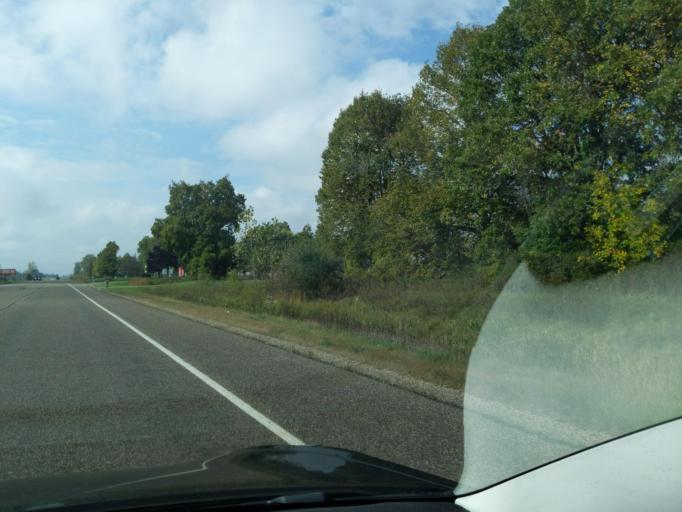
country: US
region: Michigan
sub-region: Eaton County
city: Potterville
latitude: 42.6152
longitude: -84.7530
